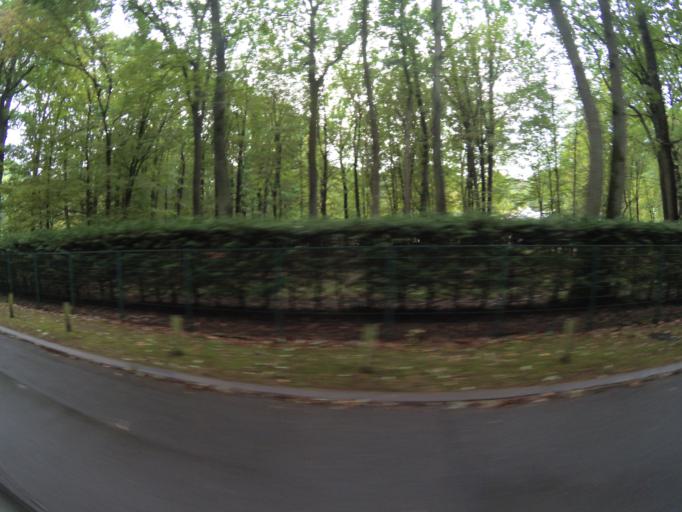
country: FR
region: Ile-de-France
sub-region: Departement de Seine-et-Marne
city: Chanteloup-en-Brie
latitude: 48.8648
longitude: 2.7326
